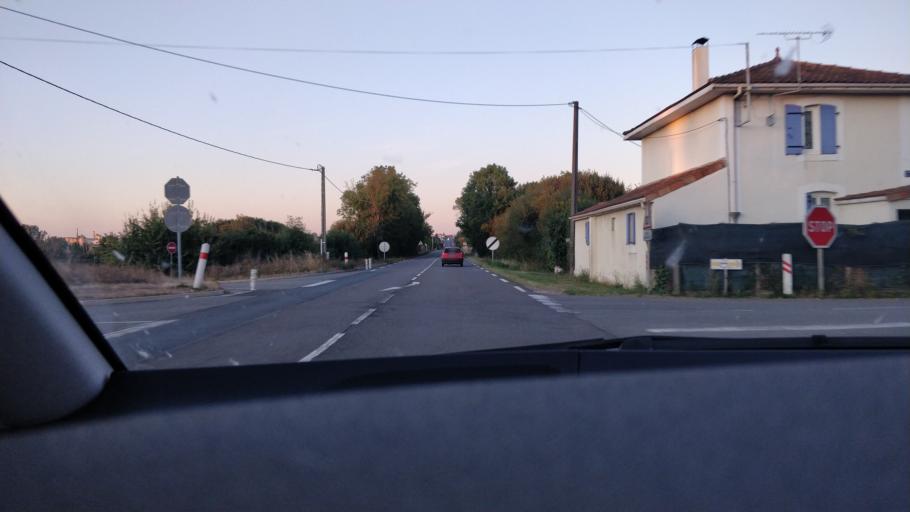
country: FR
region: Poitou-Charentes
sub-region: Departement de la Charente
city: Loubert
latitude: 45.8790
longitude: 0.5656
